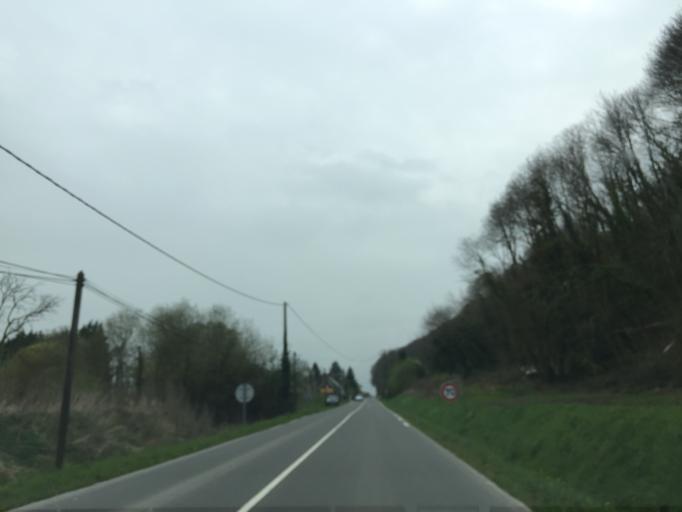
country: FR
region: Brittany
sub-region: Departement d'Ille-et-Vilaine
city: Roz-sur-Couesnon
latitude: 48.5948
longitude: -1.6006
